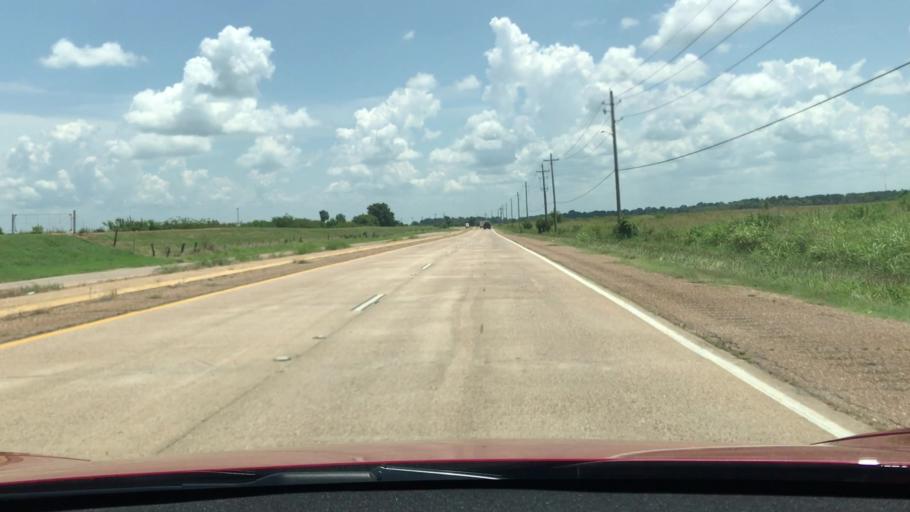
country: US
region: Louisiana
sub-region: Bossier Parish
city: Bossier City
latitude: 32.3950
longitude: -93.6881
